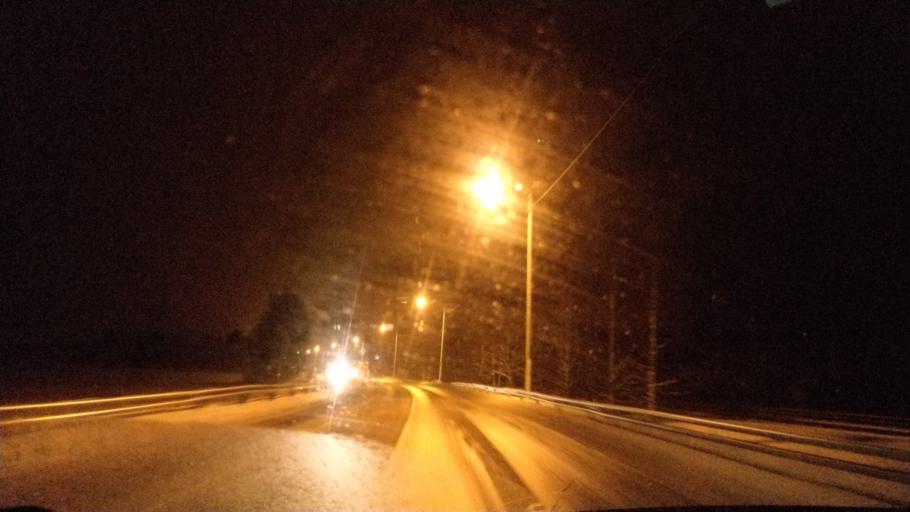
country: FI
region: Lapland
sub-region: Rovaniemi
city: Rovaniemi
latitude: 66.2861
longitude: 25.3424
